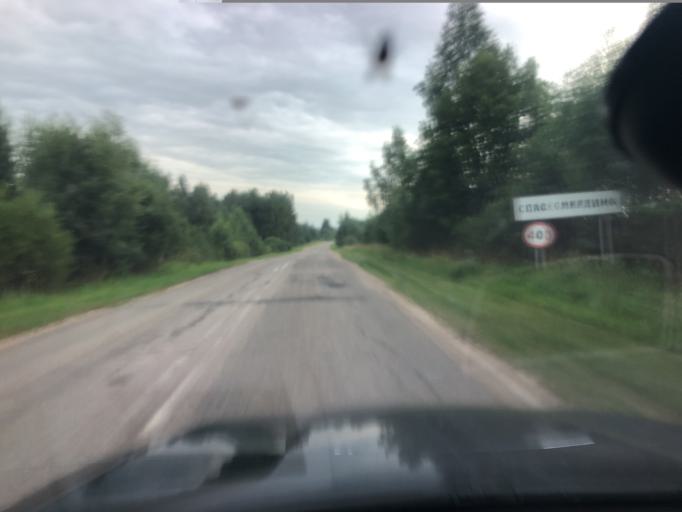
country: RU
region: Jaroslavl
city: Pereslavl'-Zalesskiy
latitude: 57.0118
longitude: 38.9692
